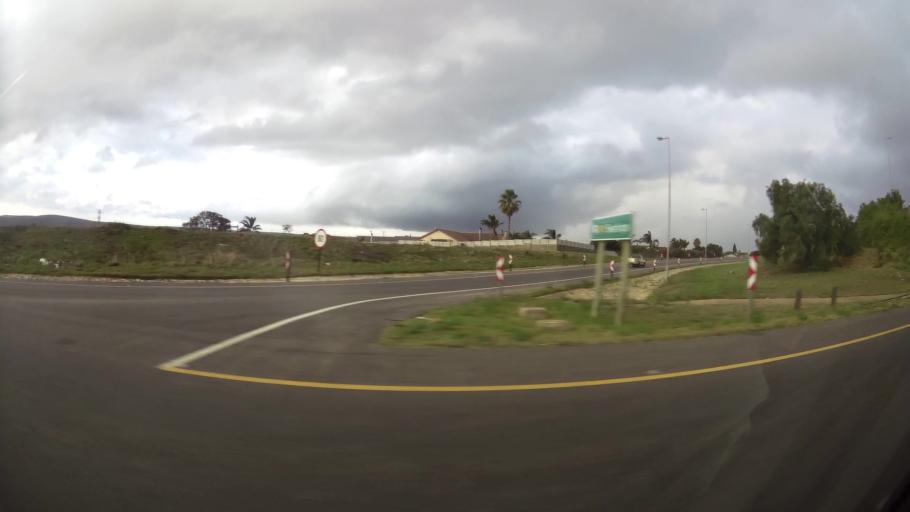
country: ZA
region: Eastern Cape
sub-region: Nelson Mandela Bay Metropolitan Municipality
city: Uitenhage
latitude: -33.8100
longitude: 25.4954
